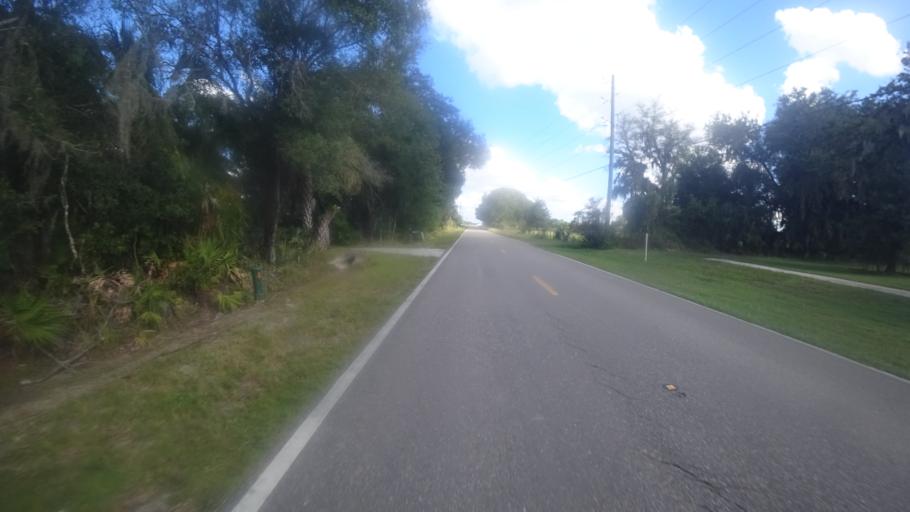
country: US
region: Florida
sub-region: Manatee County
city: Ellenton
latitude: 27.5519
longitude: -82.3760
